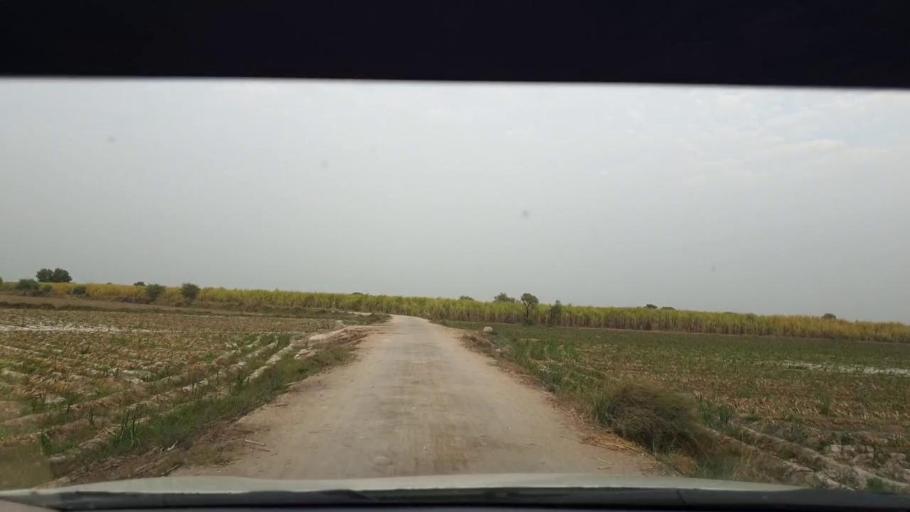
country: PK
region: Sindh
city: Sinjhoro
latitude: 25.9110
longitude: 68.7706
